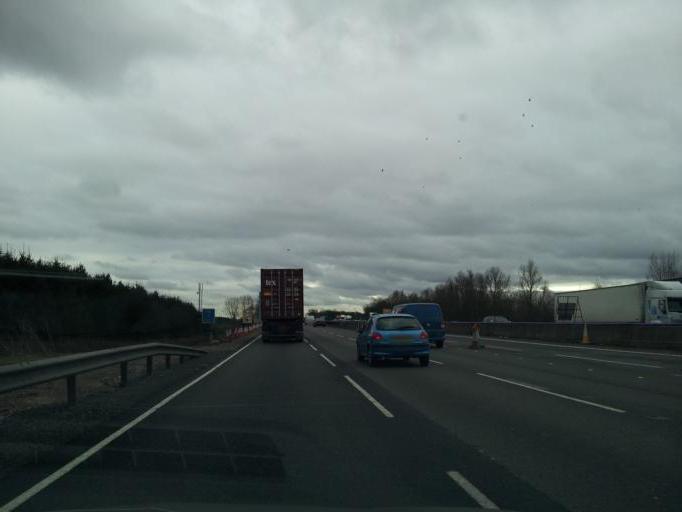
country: GB
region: England
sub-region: Staffordshire
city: Penkridge
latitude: 52.7123
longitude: -2.1010
